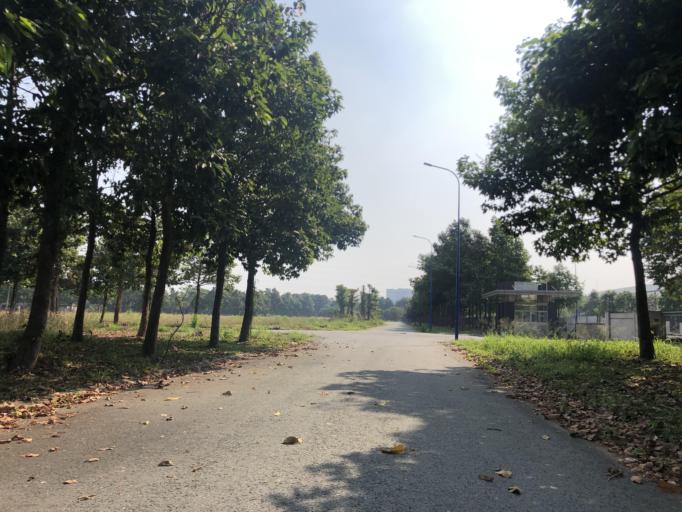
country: VN
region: Binh Duong
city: Thu Dau Mot
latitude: 11.0510
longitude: 106.6652
